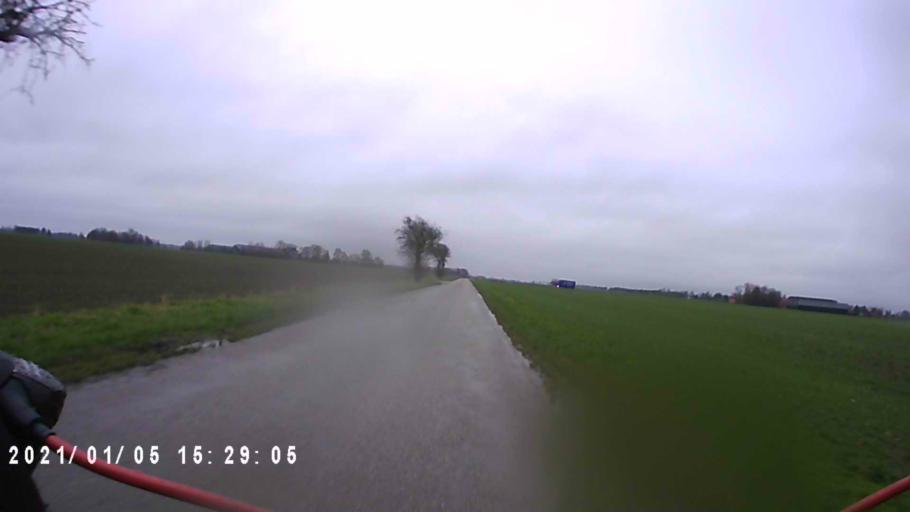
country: DE
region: Lower Saxony
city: Bunde
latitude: 53.2140
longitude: 7.1932
